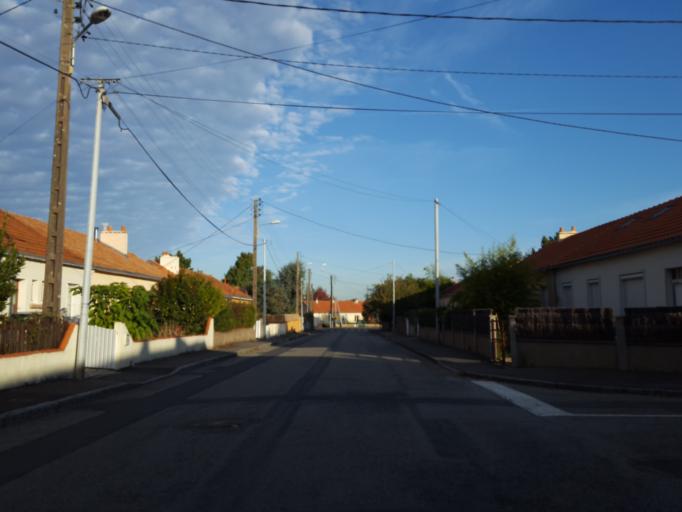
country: FR
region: Pays de la Loire
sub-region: Departement de la Loire-Atlantique
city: Saint-Sebastien-sur-Loire
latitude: 47.1988
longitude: -1.4876
